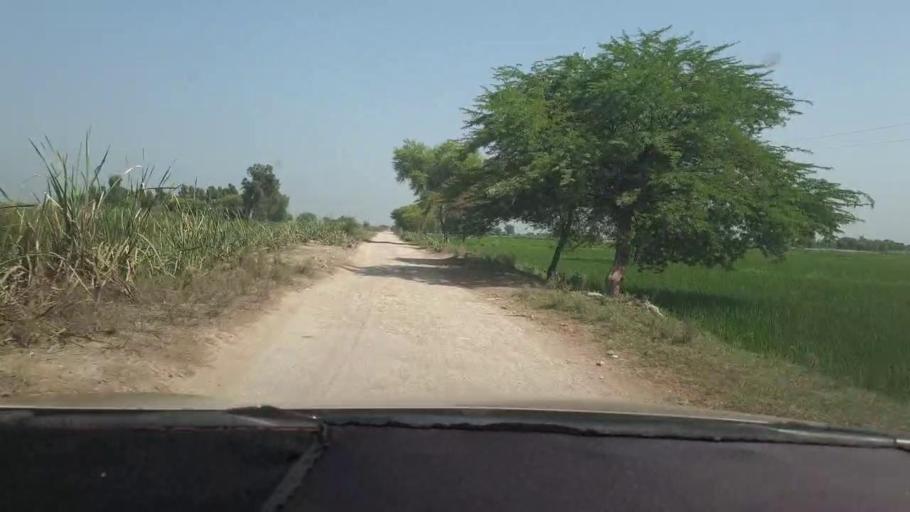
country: PK
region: Sindh
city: Miro Khan
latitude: 27.6728
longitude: 68.1390
